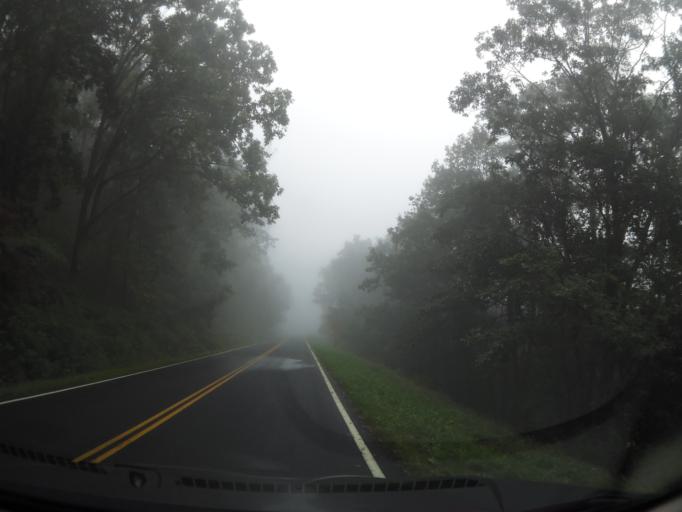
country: US
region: Virginia
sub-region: Page County
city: Luray
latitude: 38.7044
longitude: -78.3202
